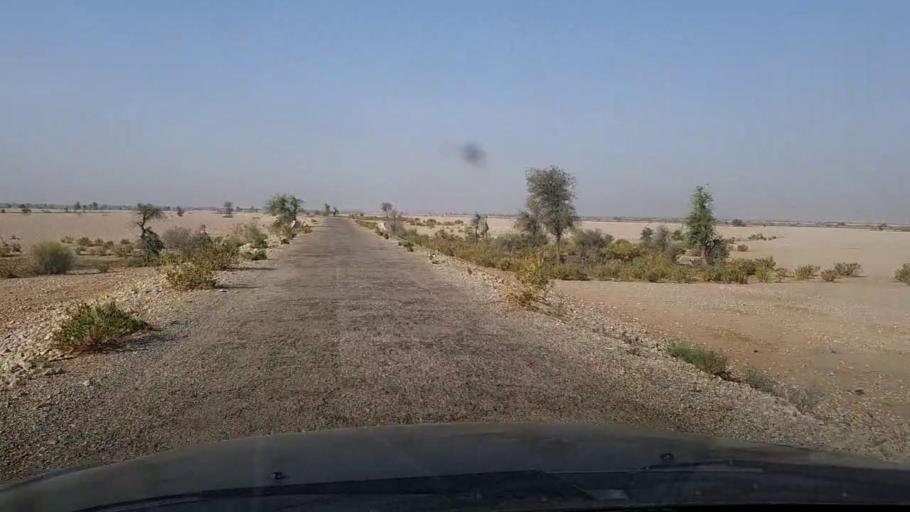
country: PK
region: Sindh
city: Sann
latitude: 25.9959
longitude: 68.0734
